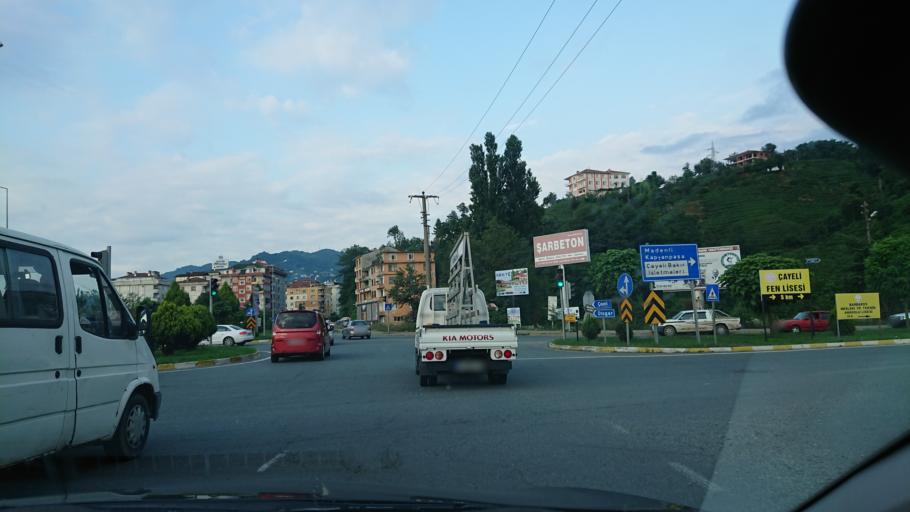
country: TR
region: Rize
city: Cayeli
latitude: 41.0838
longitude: 40.7132
